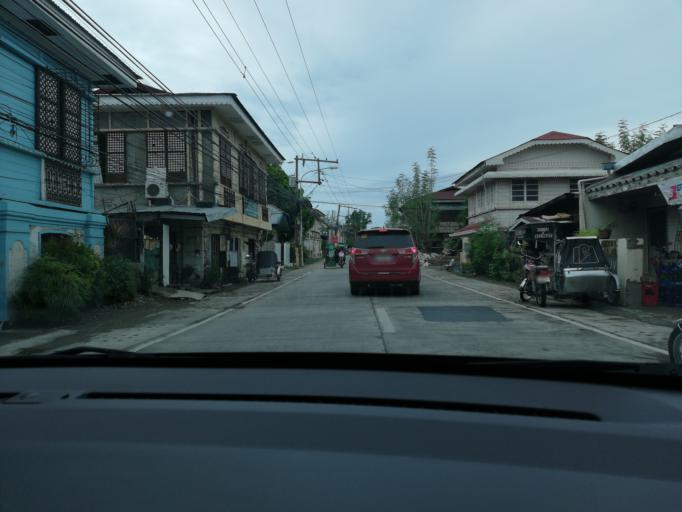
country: PH
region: Ilocos
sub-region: Province of Ilocos Sur
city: Bantay
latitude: 17.5826
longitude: 120.3863
